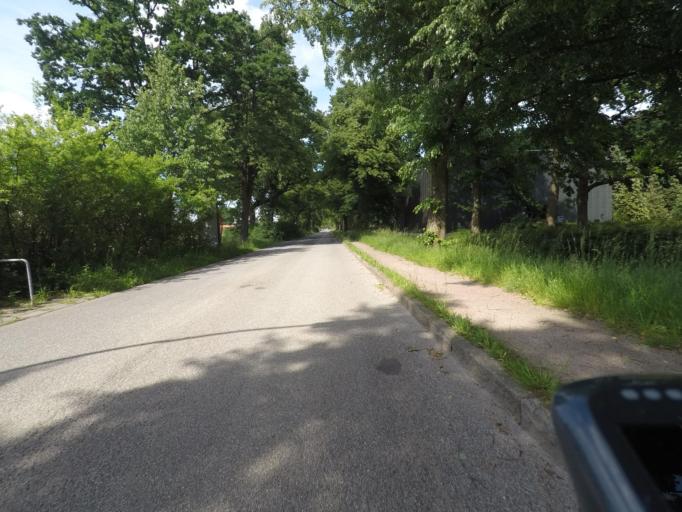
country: DE
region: Lower Saxony
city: Drage
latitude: 53.4349
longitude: 10.2316
